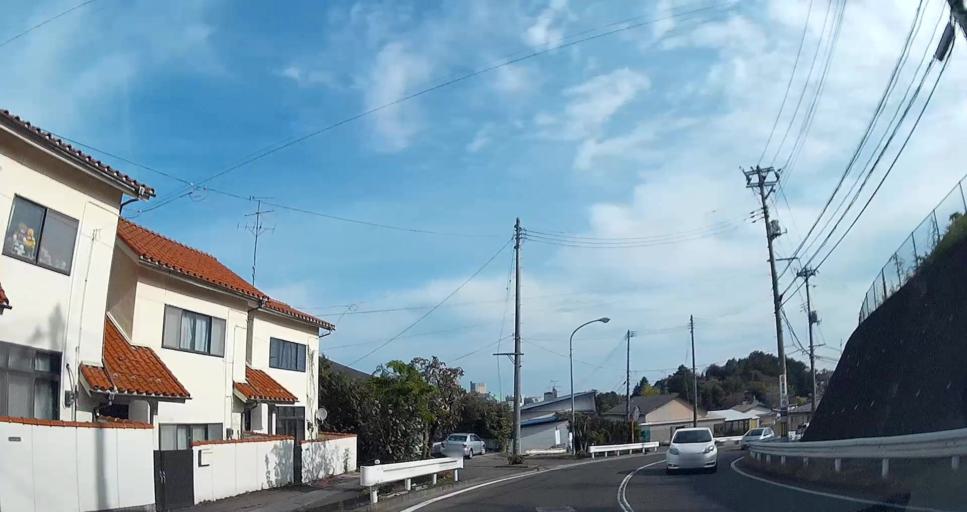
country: JP
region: Miyagi
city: Sendai
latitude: 38.2449
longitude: 140.8689
